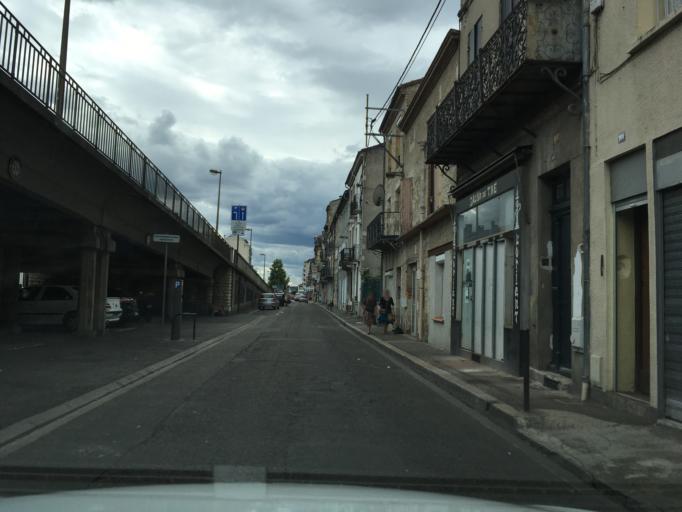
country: FR
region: Aquitaine
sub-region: Departement du Lot-et-Garonne
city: Agen
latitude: 44.2067
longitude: 0.6266
